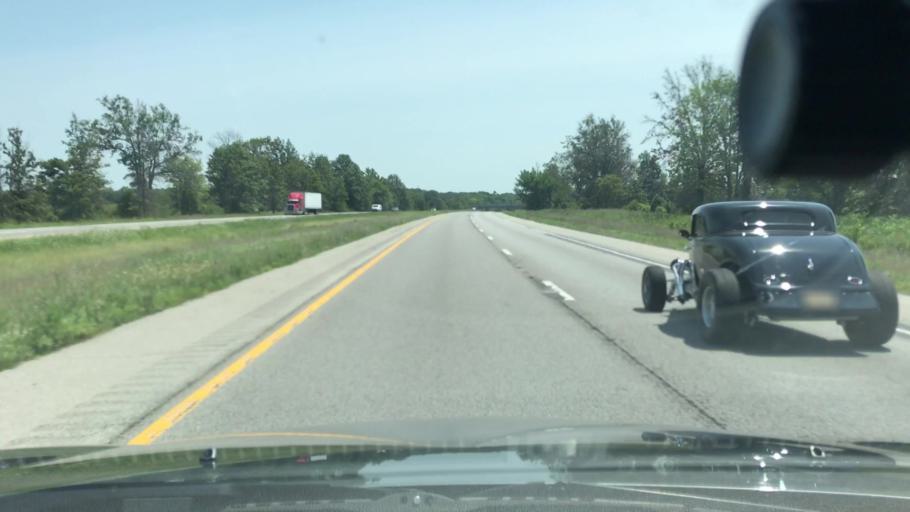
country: US
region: Illinois
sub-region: Clinton County
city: Wamac
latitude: 38.3867
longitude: -89.1350
